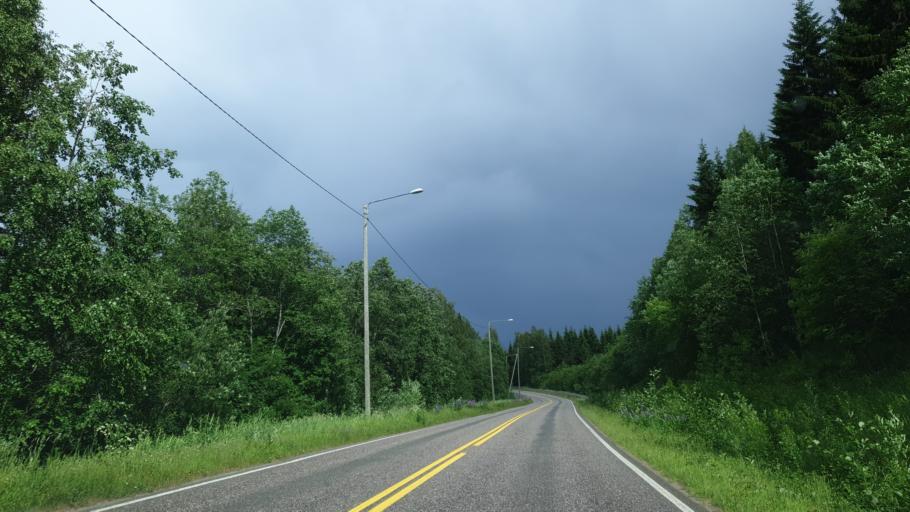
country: FI
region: Northern Savo
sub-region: Kuopio
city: Kuopio
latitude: 62.9071
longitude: 27.8492
